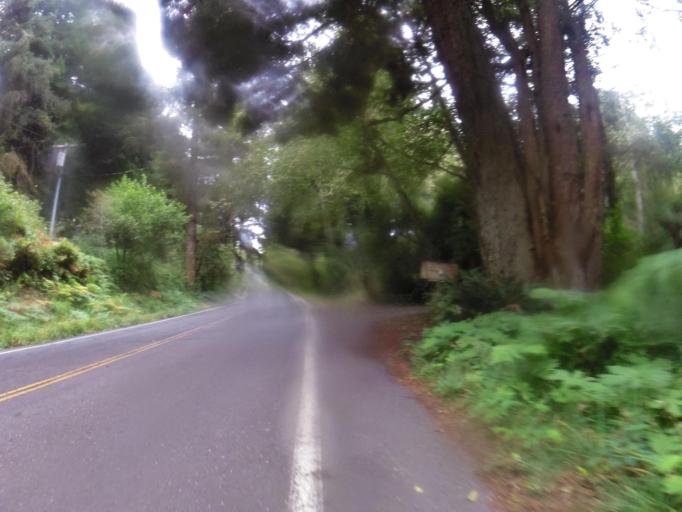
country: US
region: California
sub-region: Humboldt County
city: Westhaven-Moonstone
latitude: 41.1177
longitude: -124.1568
